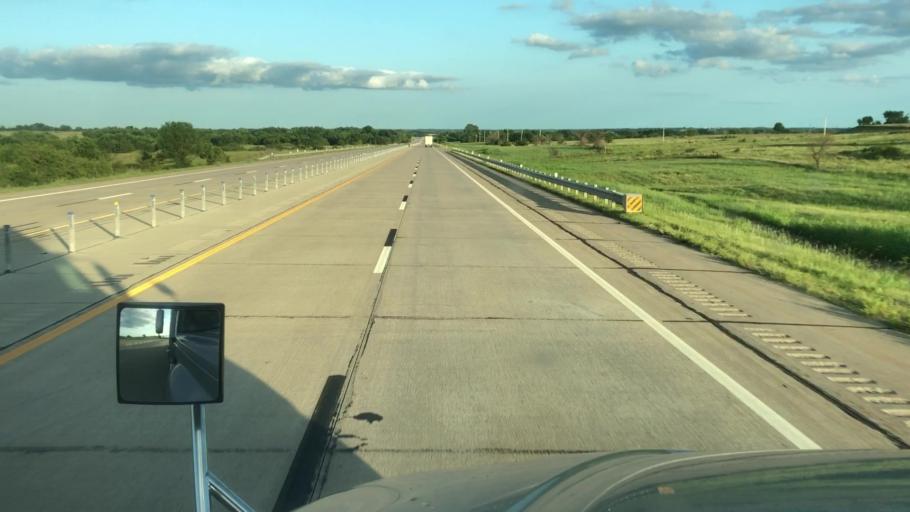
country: US
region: Oklahoma
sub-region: Pawnee County
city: Pawnee
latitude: 36.3321
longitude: -97.0133
